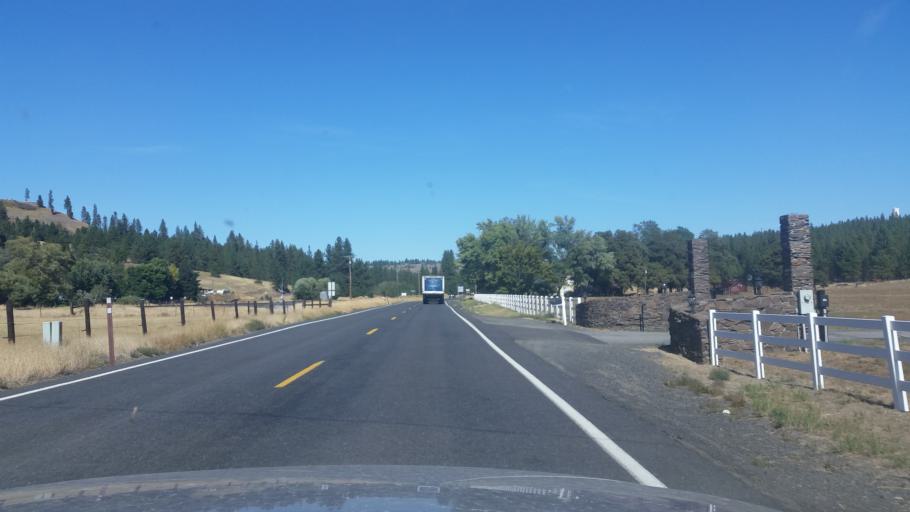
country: US
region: Washington
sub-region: Spokane County
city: Spokane
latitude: 47.5931
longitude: -117.4485
